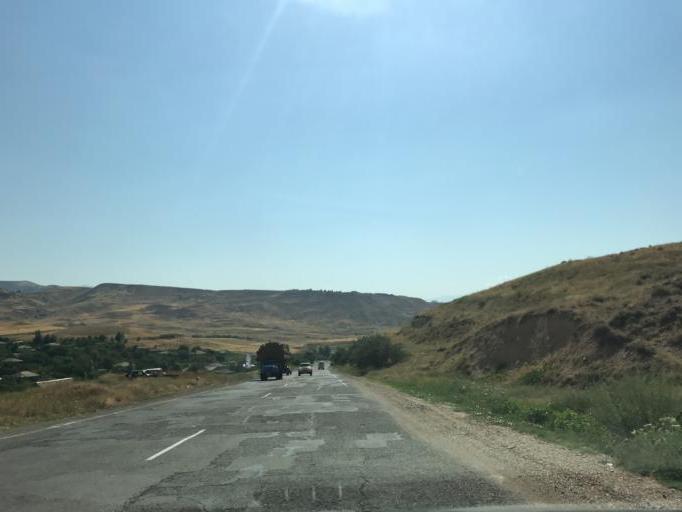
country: AM
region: Vayots' Dzori Marz
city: Rrind
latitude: 39.7620
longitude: 45.1405
